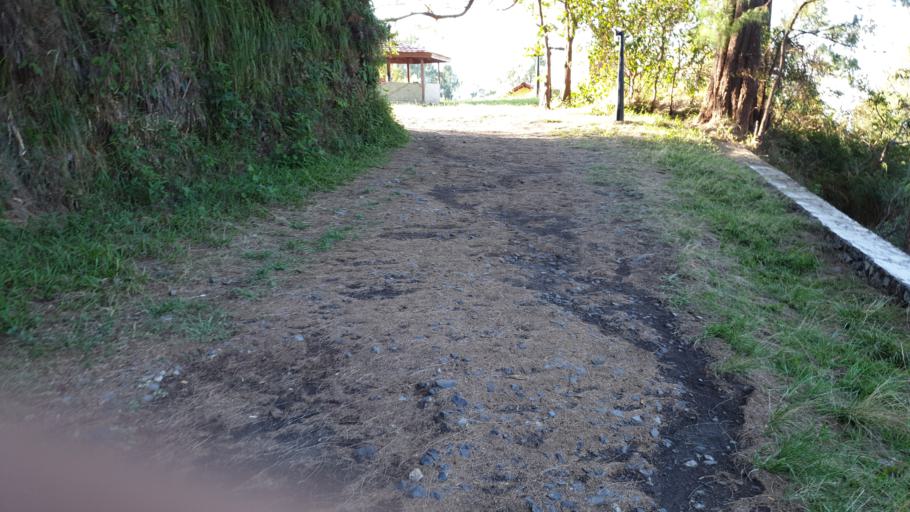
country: ID
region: East Nusa Tenggara
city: Koanara
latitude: -8.7709
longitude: 121.8151
